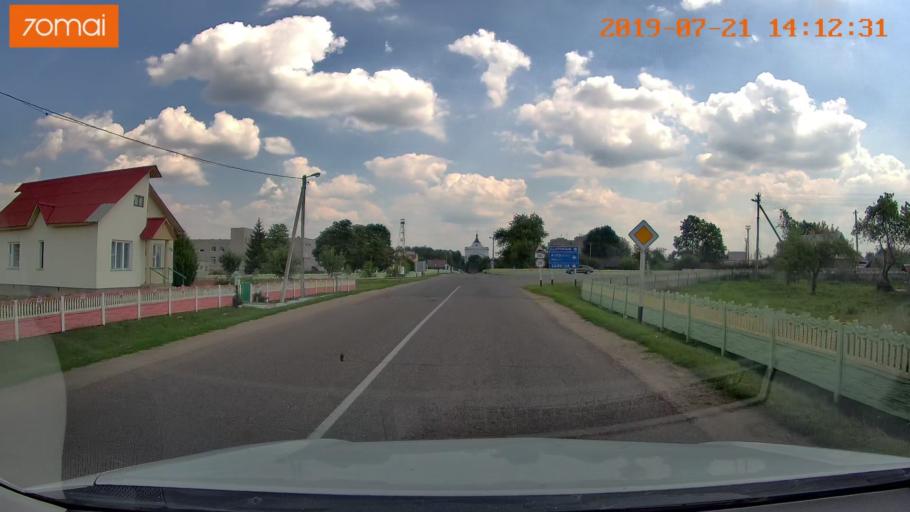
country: BY
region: Grodnenskaya
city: Karelichy
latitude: 53.6522
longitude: 26.1690
